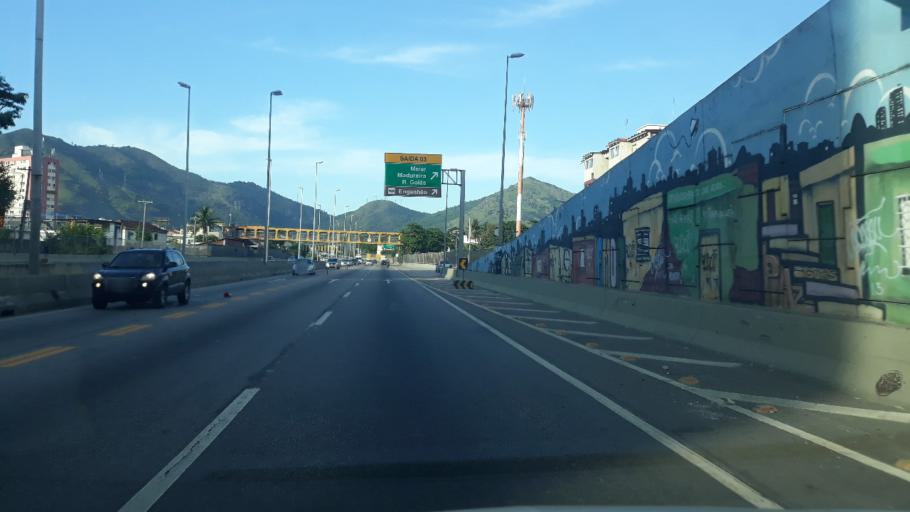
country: BR
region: Rio de Janeiro
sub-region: Rio De Janeiro
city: Rio de Janeiro
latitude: -22.8896
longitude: -43.2960
